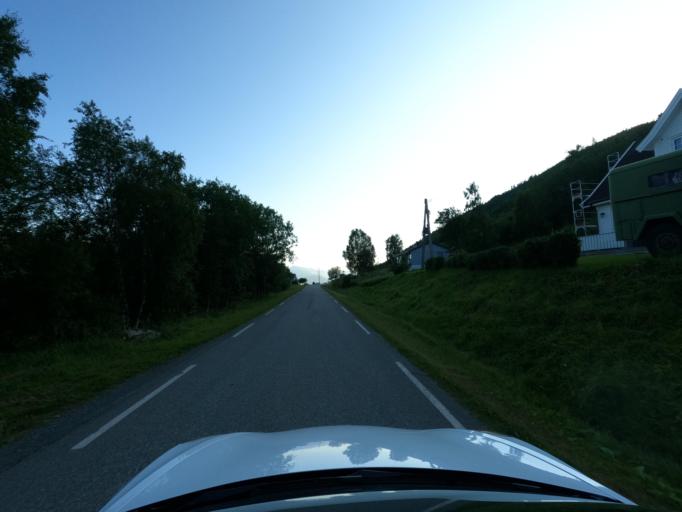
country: NO
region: Nordland
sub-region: Ballangen
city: Ballangen
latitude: 68.4655
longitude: 16.7805
